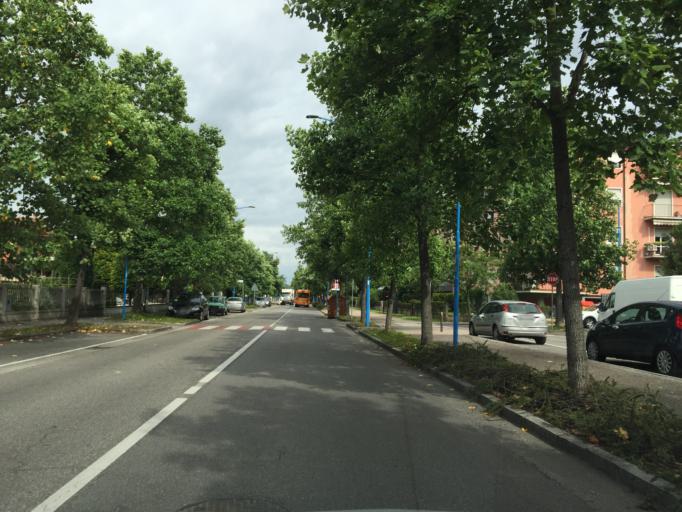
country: IT
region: Lombardy
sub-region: Provincia di Brescia
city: Folzano
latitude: 45.5129
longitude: 10.1912
